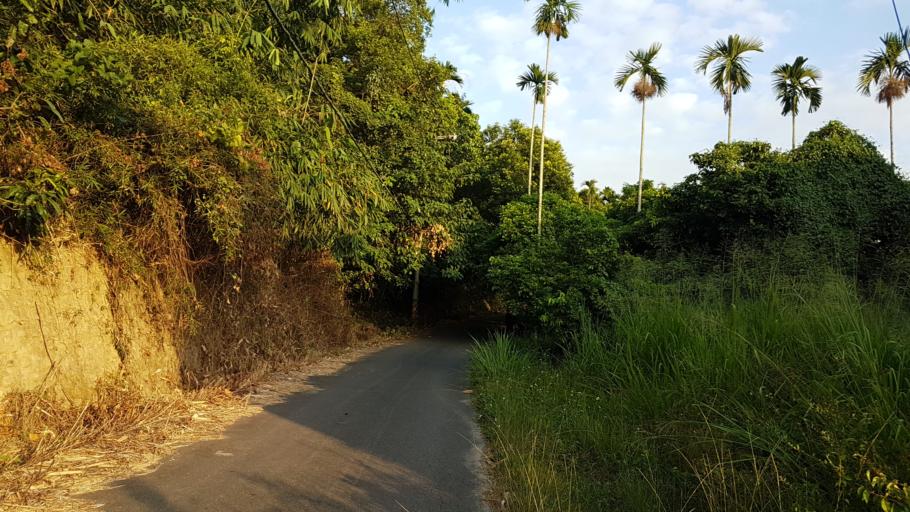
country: TW
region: Taiwan
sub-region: Chiayi
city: Jiayi Shi
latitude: 23.3673
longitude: 120.4636
